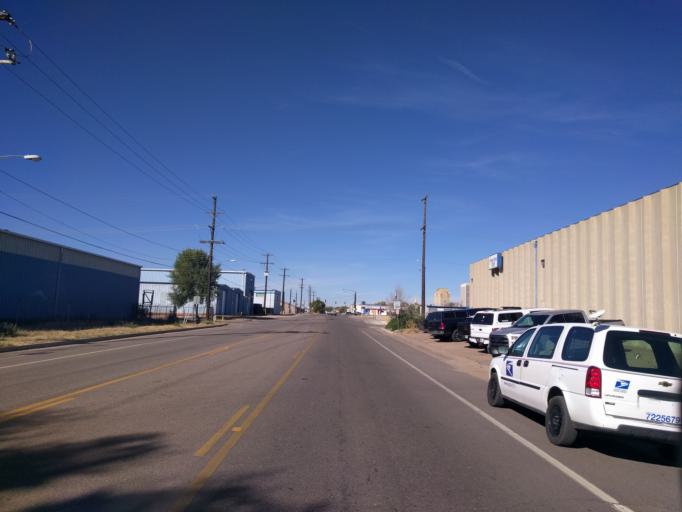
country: US
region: Colorado
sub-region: El Paso County
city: Colorado Springs
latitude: 38.8250
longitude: -104.8294
